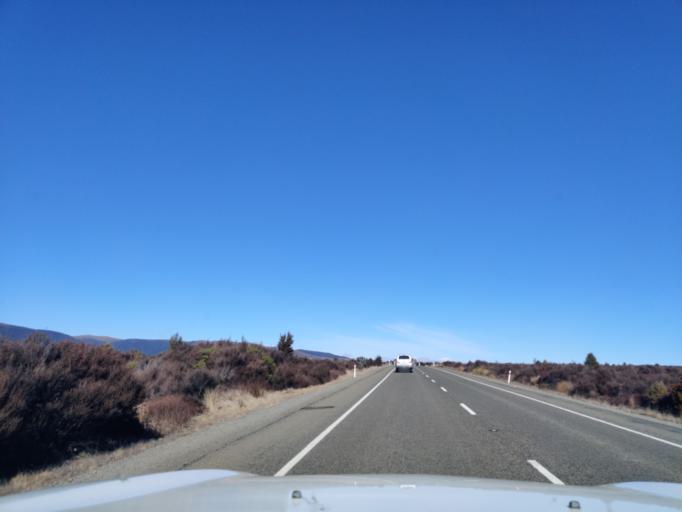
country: NZ
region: Waikato
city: Turangi
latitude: -39.2284
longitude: 175.7352
